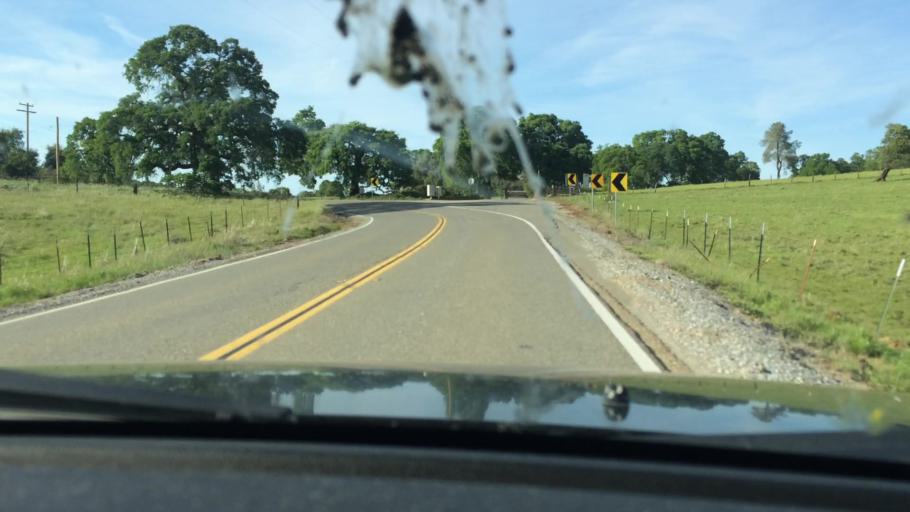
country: US
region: California
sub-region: Amador County
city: Plymouth
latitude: 38.4946
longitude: -120.9359
